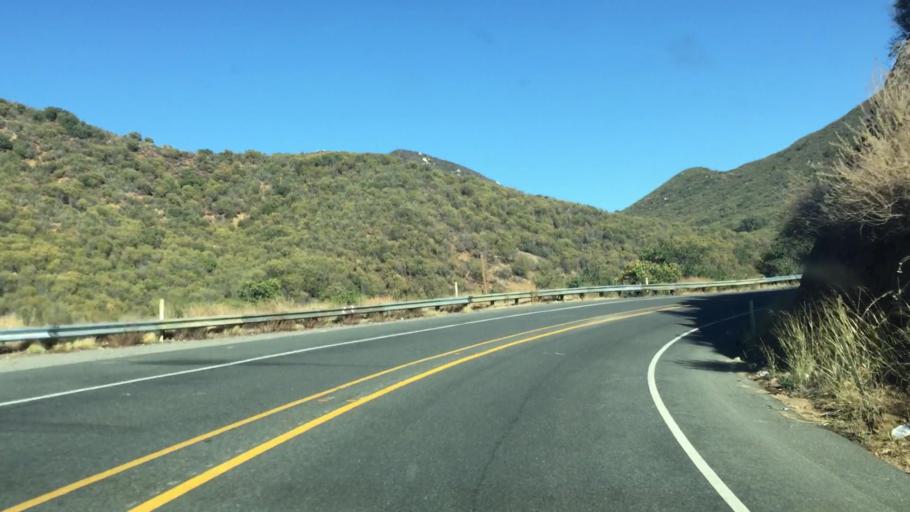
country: US
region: California
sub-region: Orange County
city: Coto De Caza
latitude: 33.5968
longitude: -117.4641
